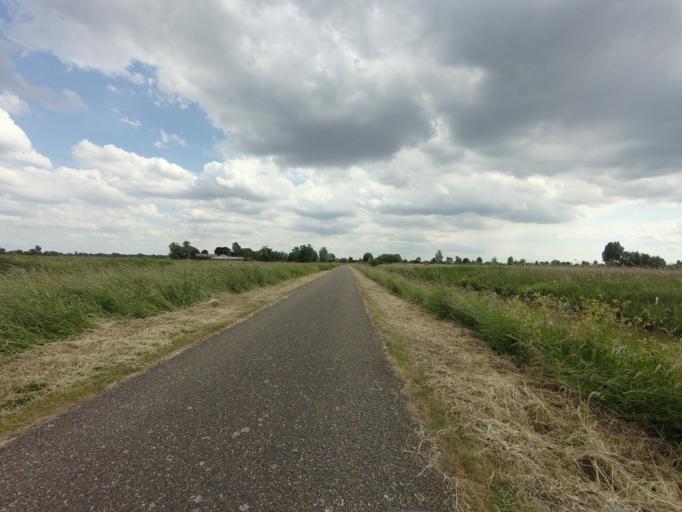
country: NL
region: Utrecht
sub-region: Stichtse Vecht
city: Maarssen
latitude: 52.1592
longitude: 5.0505
